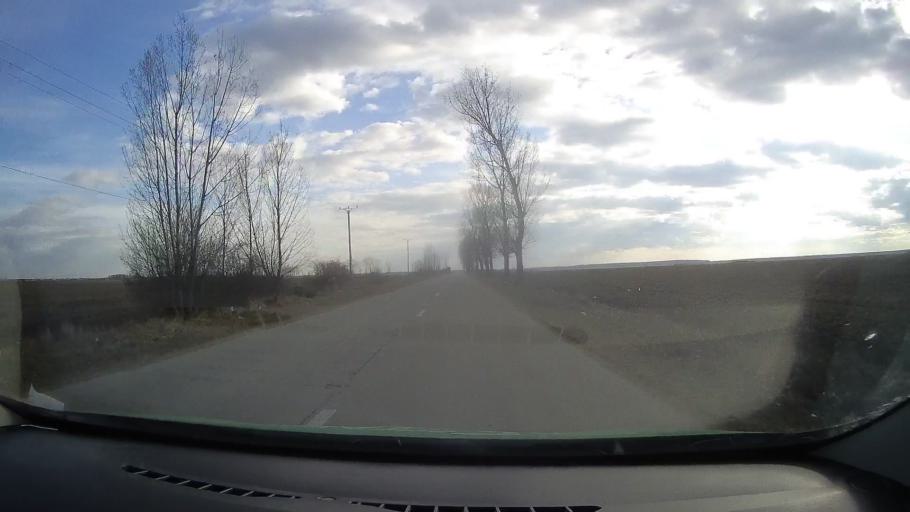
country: RO
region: Dambovita
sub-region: Comuna Vacaresti
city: Vacaresti
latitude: 44.8789
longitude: 25.4635
